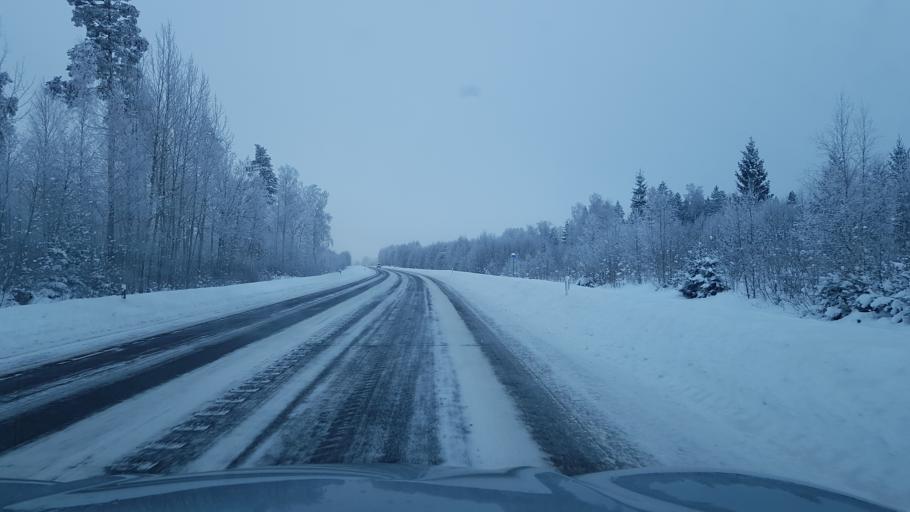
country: EE
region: Ida-Virumaa
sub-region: Johvi vald
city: Johvi
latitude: 59.2202
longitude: 27.3375
